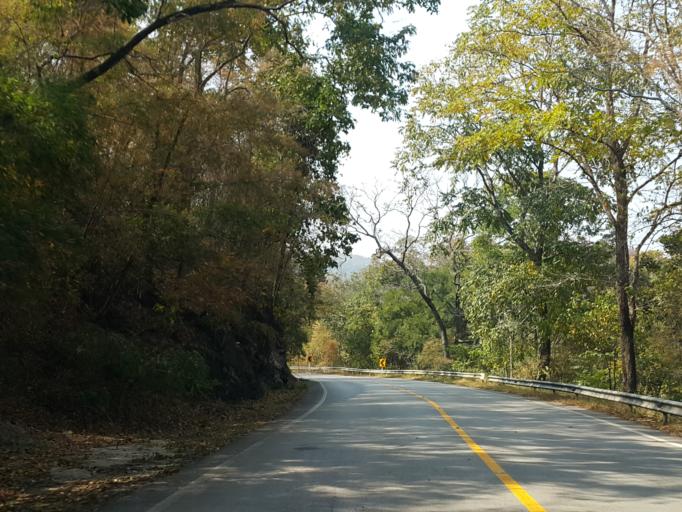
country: TH
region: Chiang Mai
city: Hot
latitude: 18.2290
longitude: 98.5062
